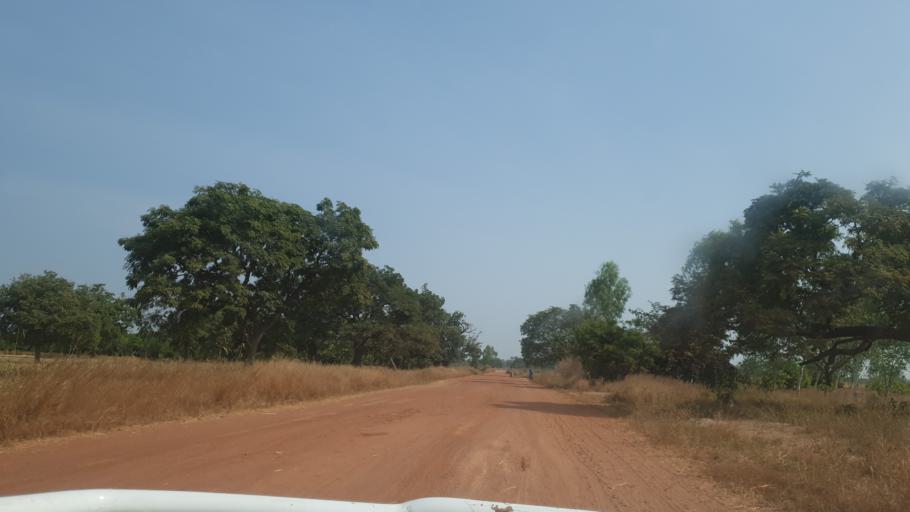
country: ML
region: Koulikoro
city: Dioila
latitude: 12.2264
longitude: -6.2157
